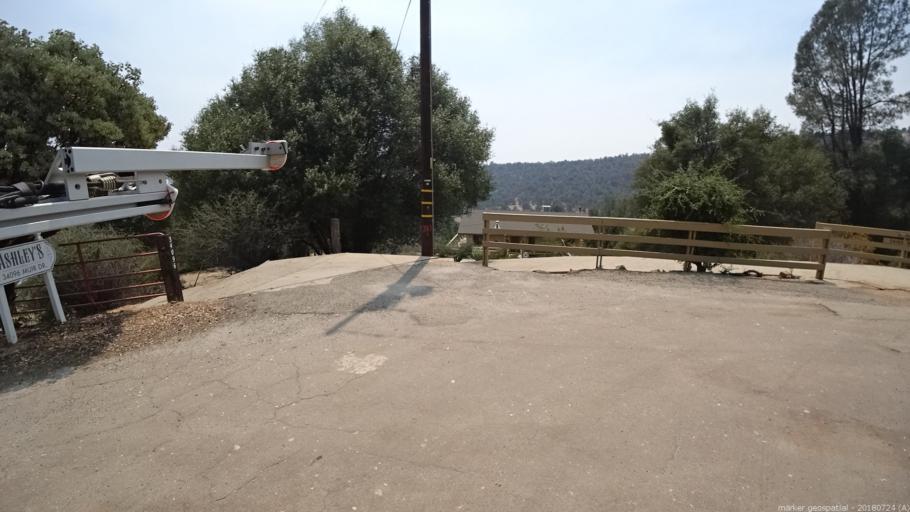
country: US
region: California
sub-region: Madera County
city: Oakhurst
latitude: 37.2434
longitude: -119.5561
